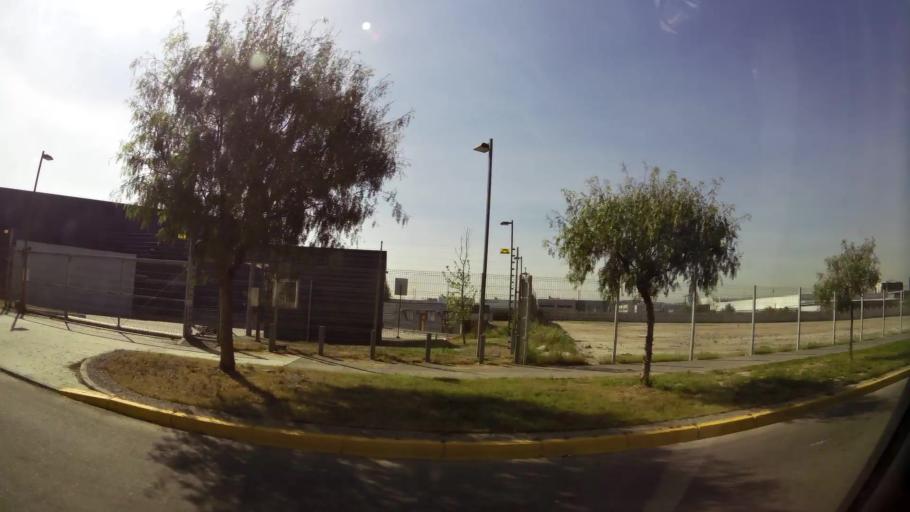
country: CL
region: Santiago Metropolitan
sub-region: Provincia de Santiago
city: Lo Prado
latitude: -33.4247
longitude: -70.7788
